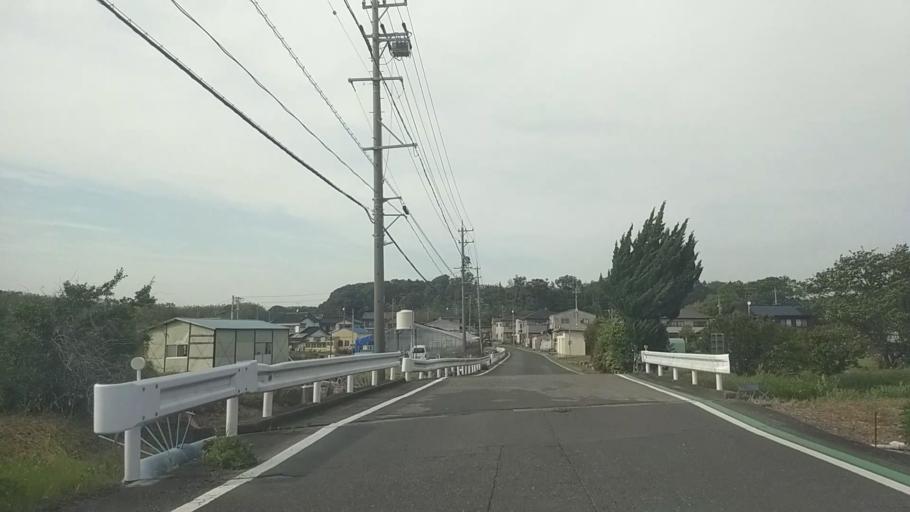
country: JP
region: Shizuoka
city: Kosai-shi
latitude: 34.7421
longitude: 137.6140
